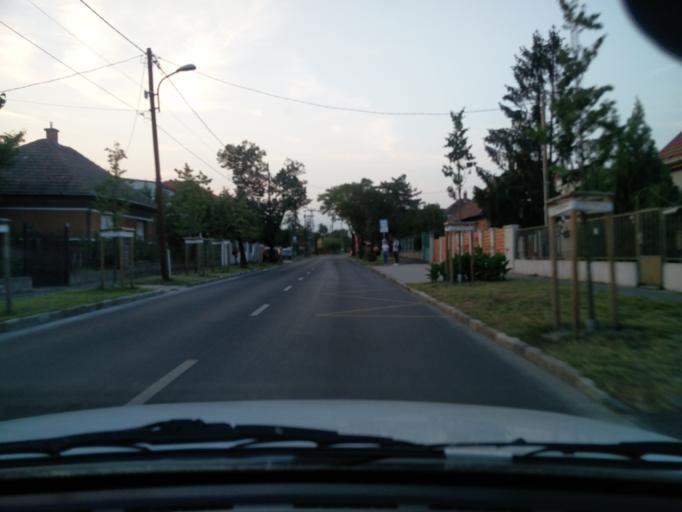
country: HU
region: Budapest
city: Budapest XXIII. keruelet
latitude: 47.3950
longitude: 19.1006
